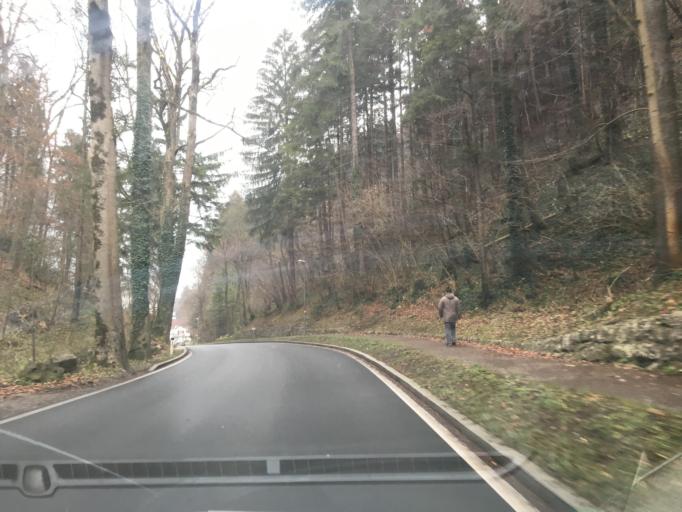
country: AT
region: Vorarlberg
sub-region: Politischer Bezirk Feldkirch
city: Gotzis
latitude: 47.3283
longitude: 9.6456
